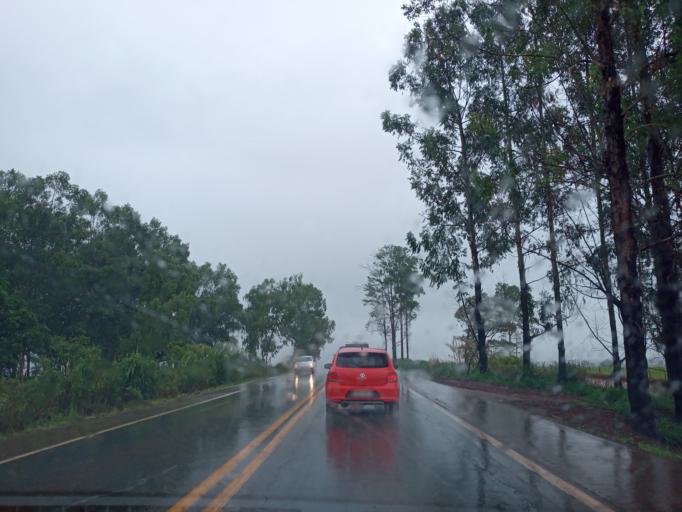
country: BR
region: Minas Gerais
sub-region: Luz
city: Luz
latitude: -19.7761
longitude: -45.7507
